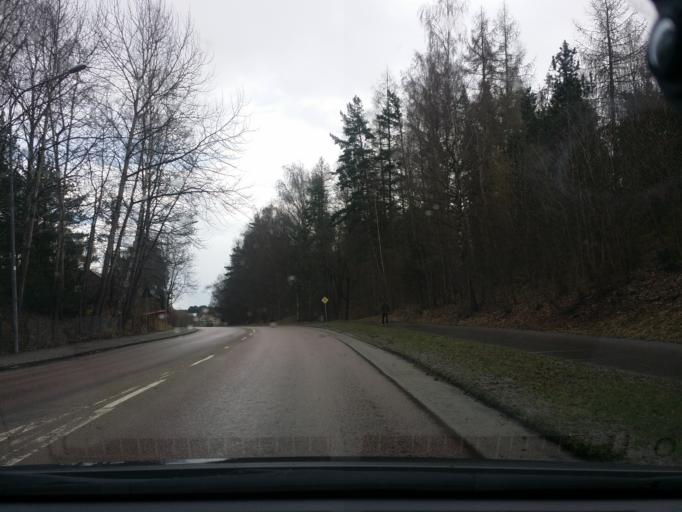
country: SE
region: Uppsala
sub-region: Enkopings Kommun
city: Enkoping
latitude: 59.6437
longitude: 17.0882
